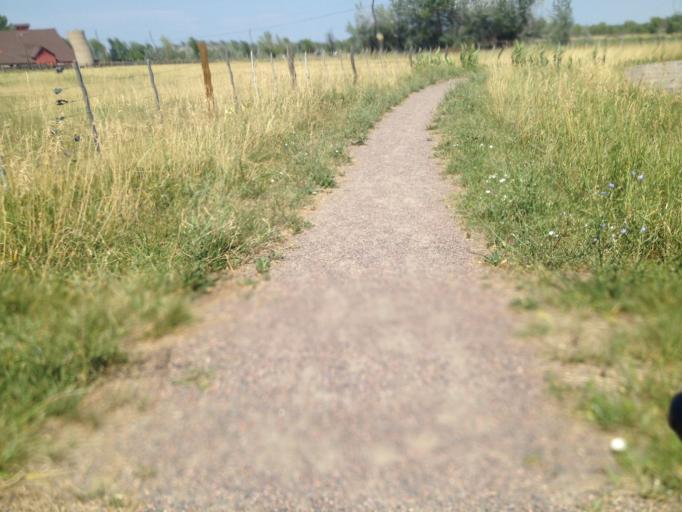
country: US
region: Colorado
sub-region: Boulder County
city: Superior
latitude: 39.9833
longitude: -105.2137
